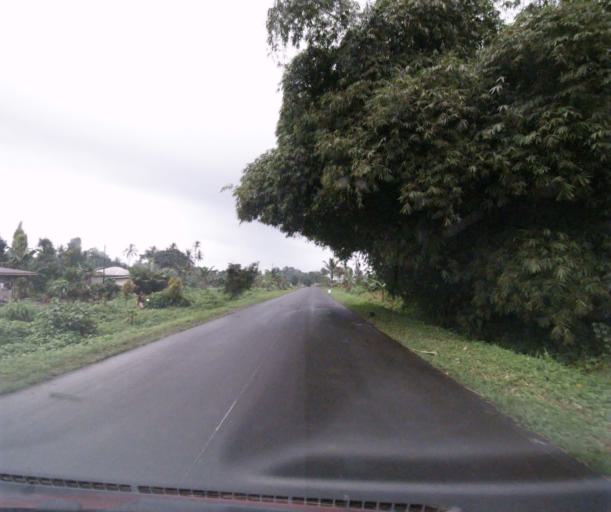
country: CM
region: South-West Province
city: Idenao
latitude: 4.1327
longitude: 8.9885
